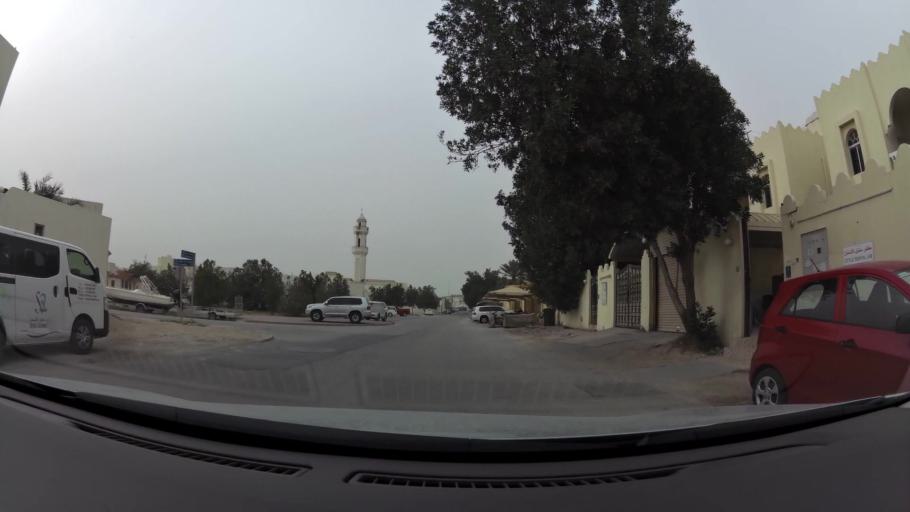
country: QA
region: Baladiyat ad Dawhah
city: Doha
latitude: 25.2565
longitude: 51.4938
